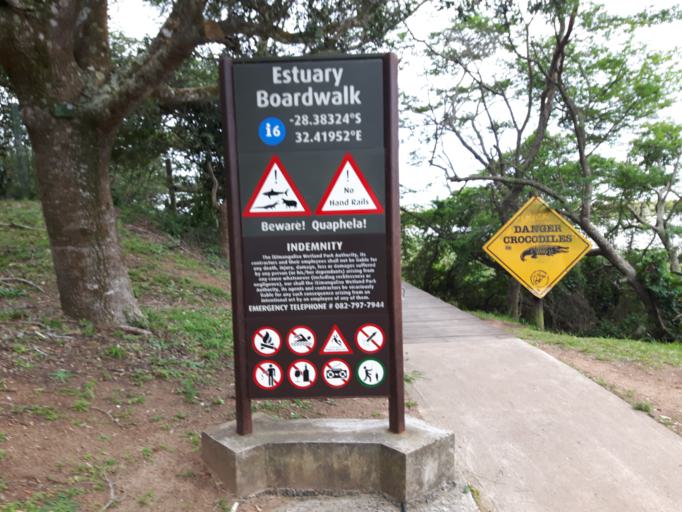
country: ZA
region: KwaZulu-Natal
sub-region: uMkhanyakude District Municipality
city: Mtubatuba
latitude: -28.3833
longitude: 32.4194
